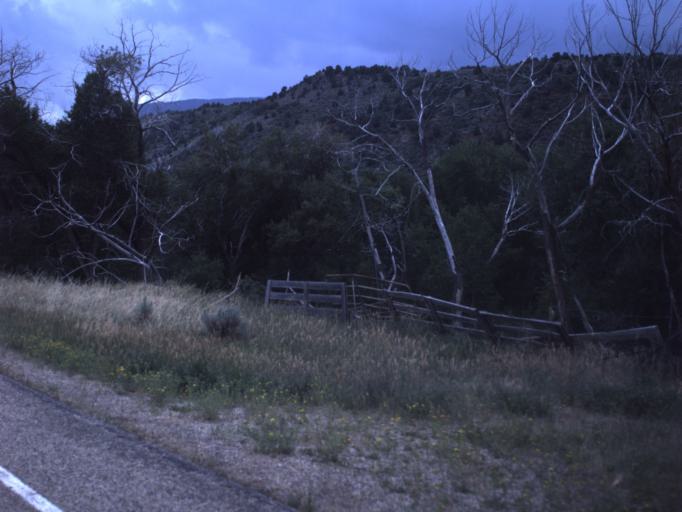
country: US
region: Utah
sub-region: Duchesne County
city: Duchesne
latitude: 40.4373
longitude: -110.8109
